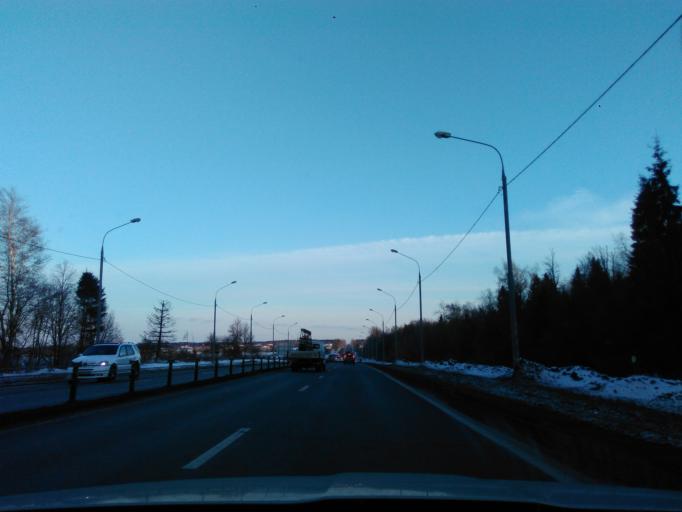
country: RU
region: Moskovskaya
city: Klin
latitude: 56.2949
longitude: 36.8038
